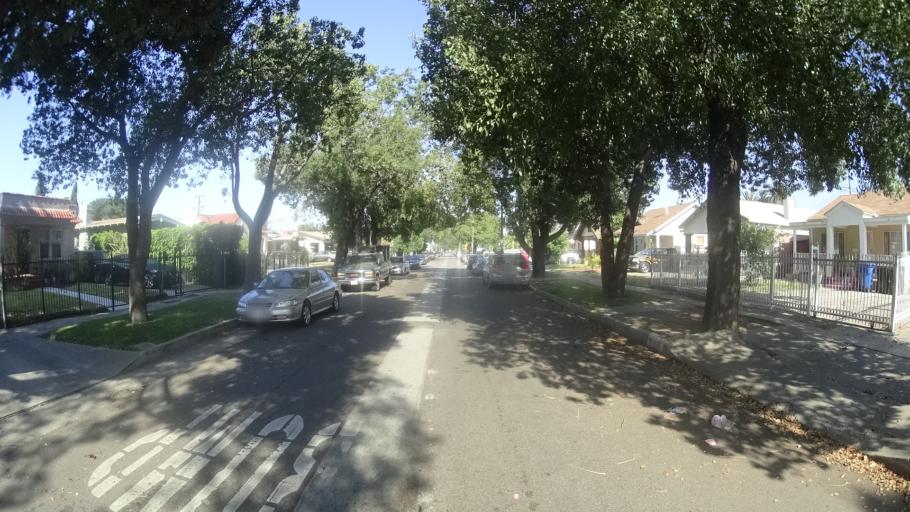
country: US
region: California
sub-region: Los Angeles County
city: Westmont
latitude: 33.9762
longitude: -118.2947
